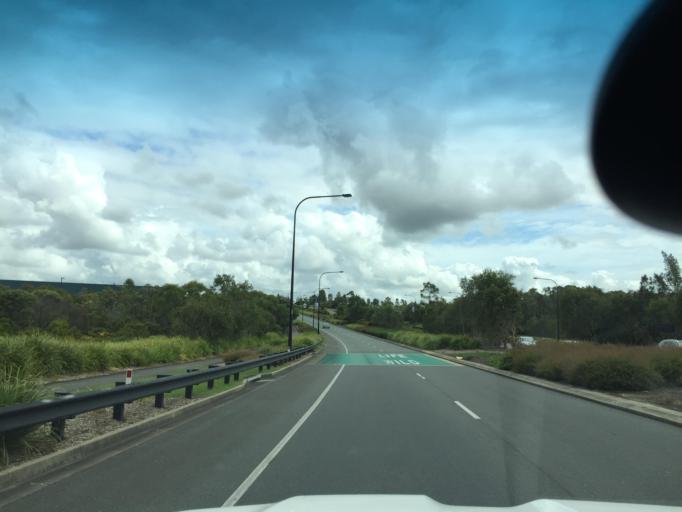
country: AU
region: Queensland
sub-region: Moreton Bay
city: Deception Bay
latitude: -27.2136
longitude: 152.9996
